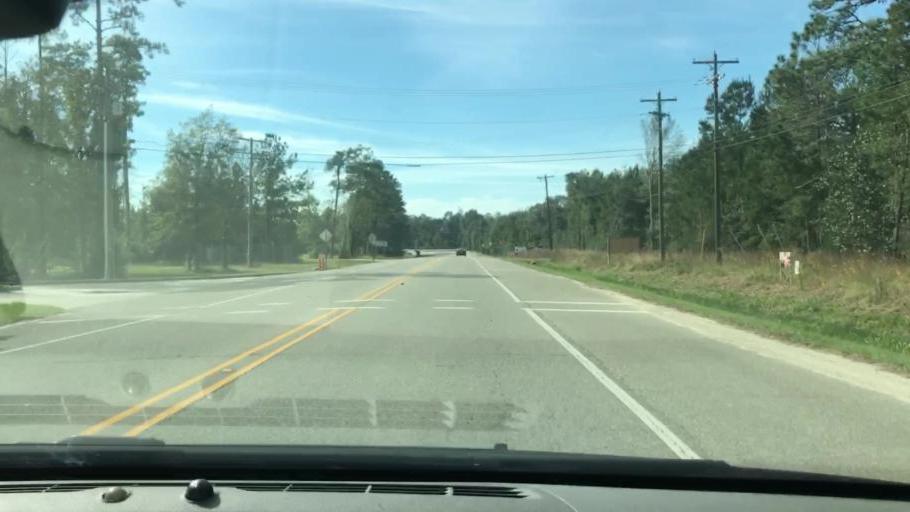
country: US
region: Louisiana
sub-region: Saint Tammany Parish
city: Pearl River
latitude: 30.3830
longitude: -89.7666
